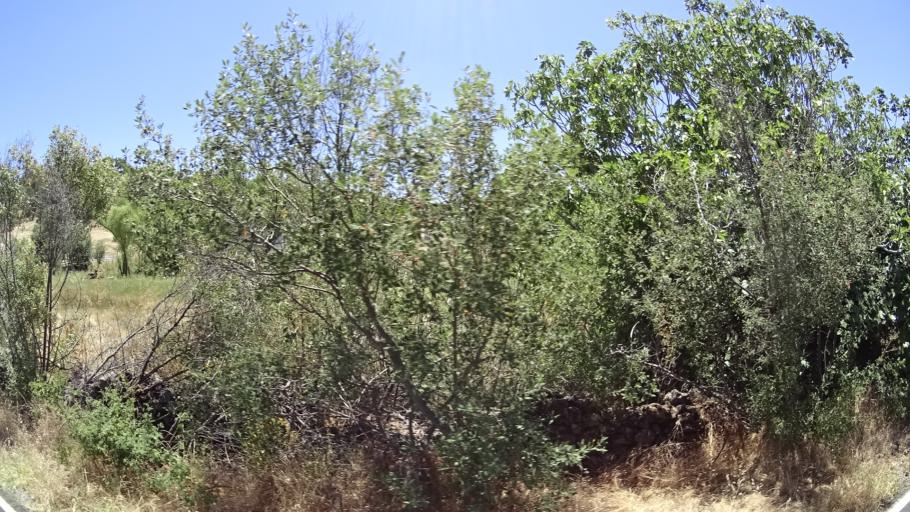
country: US
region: California
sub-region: Calaveras County
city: Valley Springs
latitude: 38.2317
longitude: -120.8015
